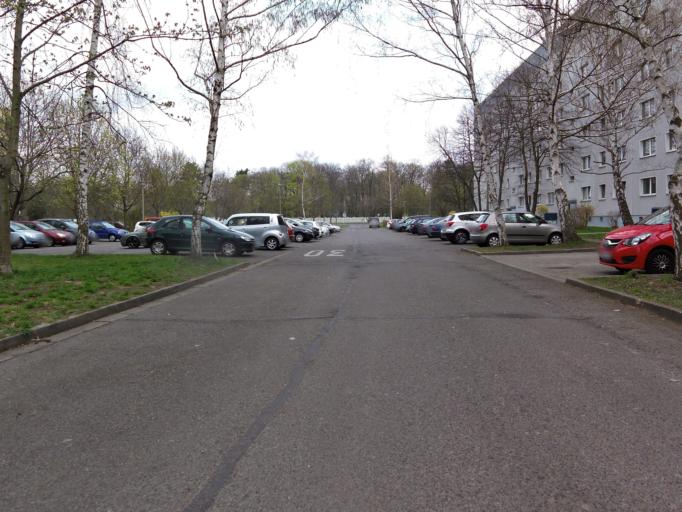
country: DE
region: Saxony
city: Leipzig
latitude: 51.3154
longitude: 12.2981
